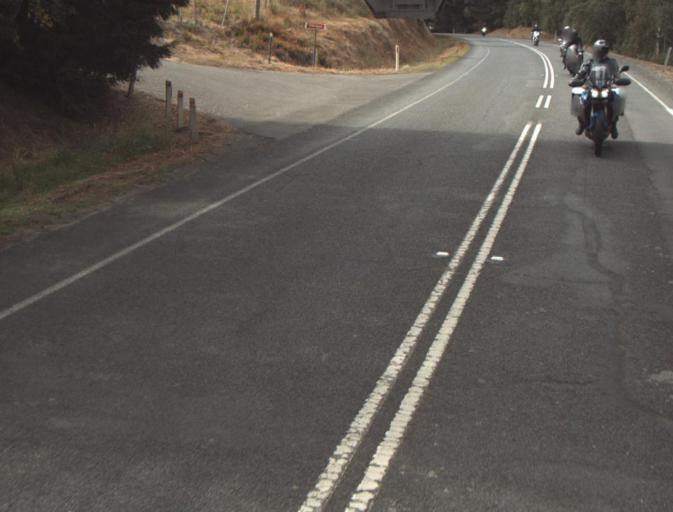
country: AU
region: Tasmania
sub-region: Launceston
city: Mayfield
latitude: -41.2700
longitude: 147.2143
